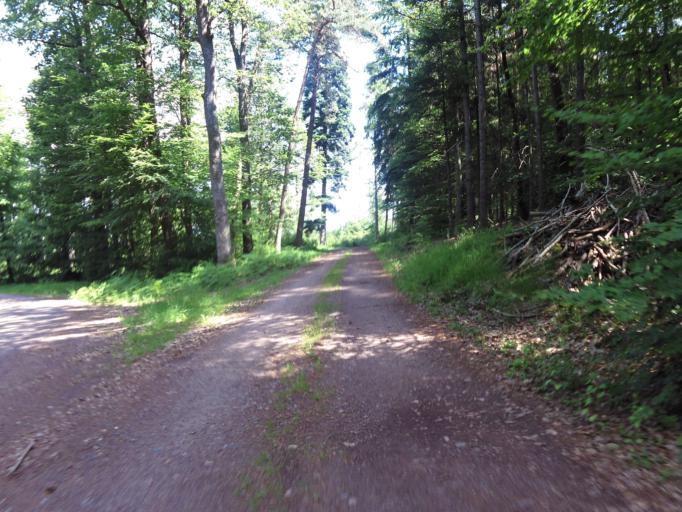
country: DE
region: Rheinland-Pfalz
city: Eusserthal
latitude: 49.2961
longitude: 7.9591
